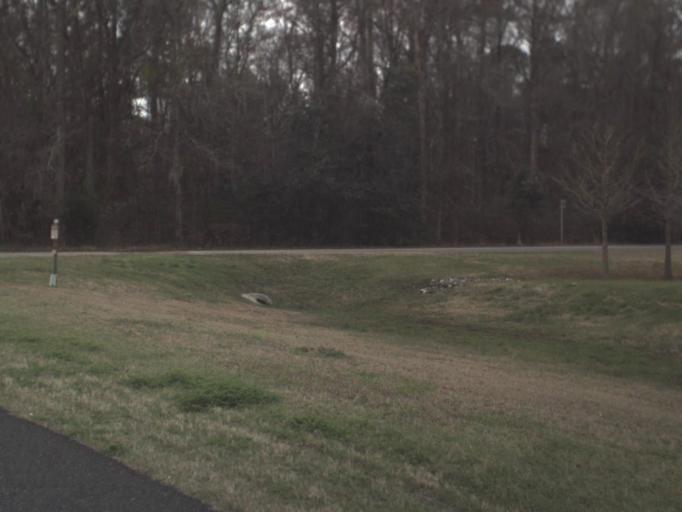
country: US
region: Florida
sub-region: Jefferson County
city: Monticello
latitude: 30.3757
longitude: -83.8116
